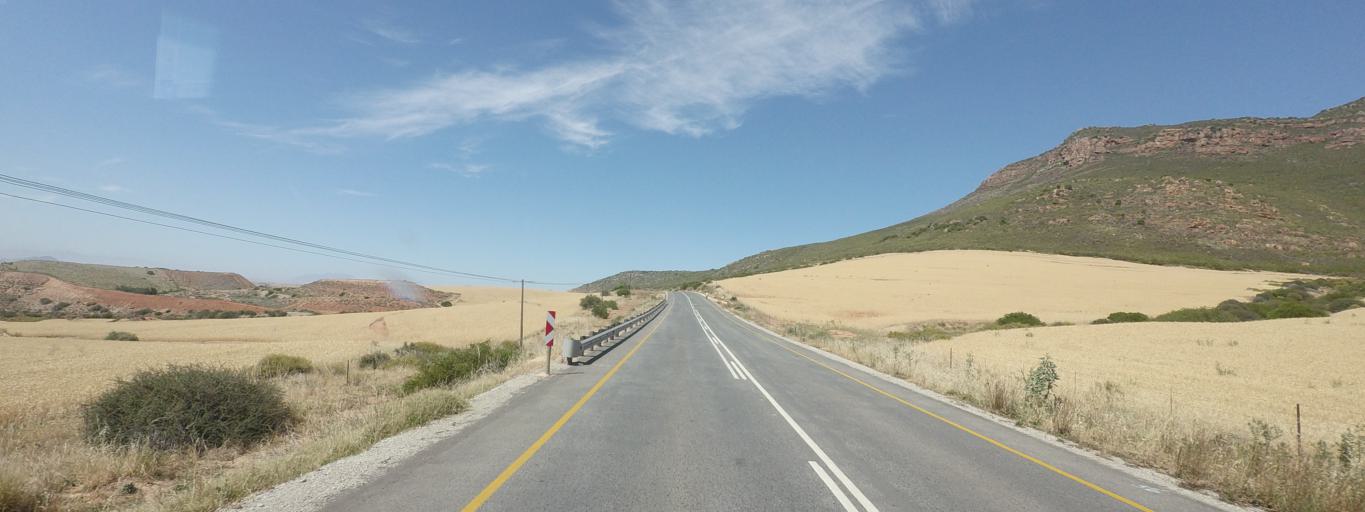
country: ZA
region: Western Cape
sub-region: West Coast District Municipality
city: Piketberg
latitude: -32.9222
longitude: 18.7575
